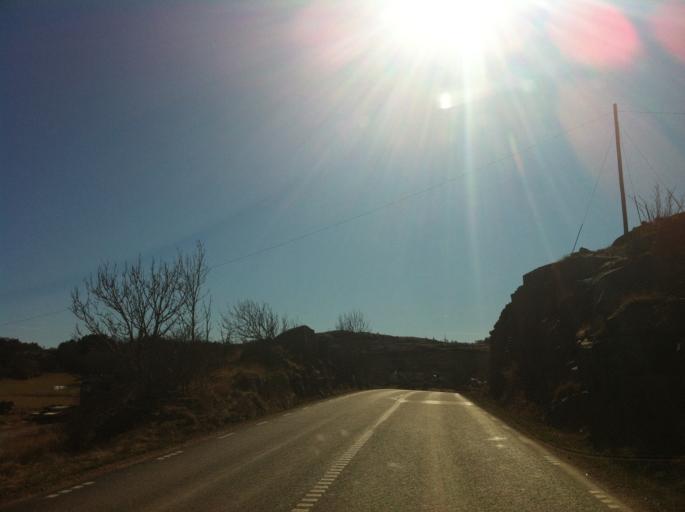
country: SE
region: Vaestra Goetaland
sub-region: Sotenas Kommun
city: Hunnebostrand
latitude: 58.4128
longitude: 11.3176
